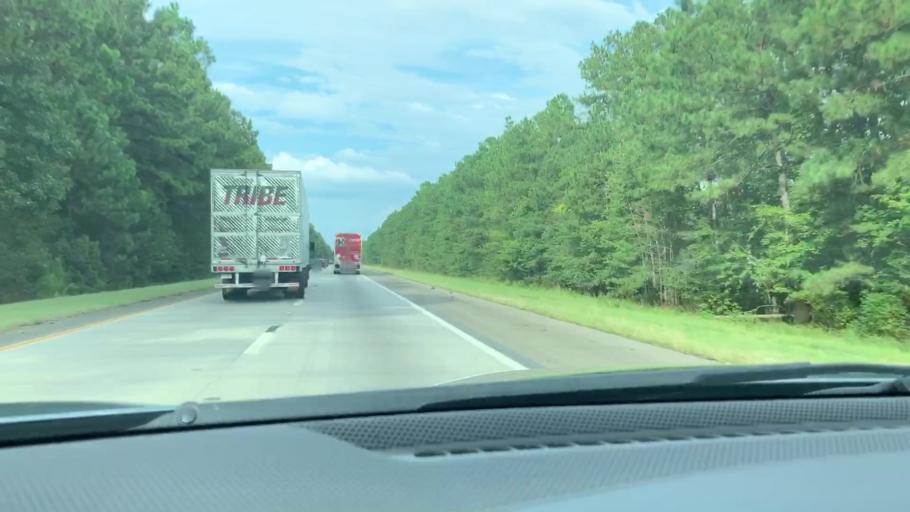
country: US
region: South Carolina
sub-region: Colleton County
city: Walterboro
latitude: 33.0561
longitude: -80.6651
